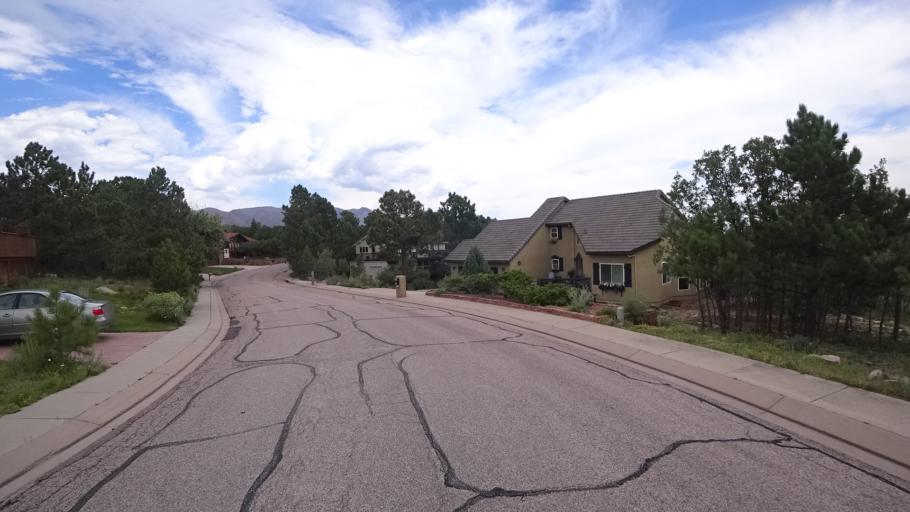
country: US
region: Colorado
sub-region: El Paso County
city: Colorado Springs
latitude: 38.9039
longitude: -104.8471
